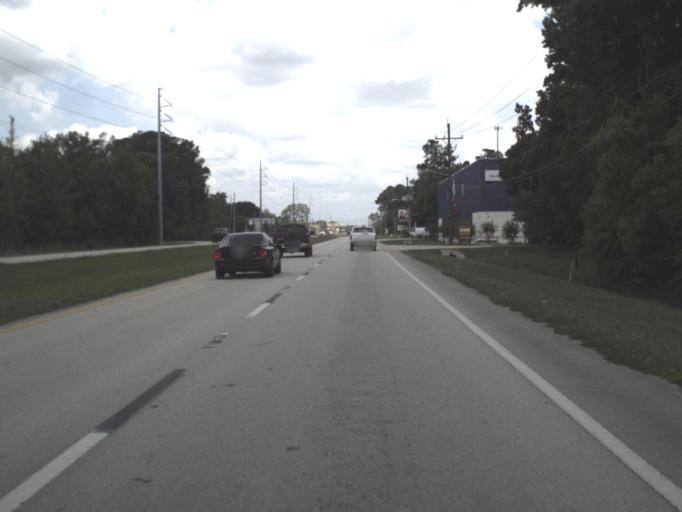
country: US
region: Florida
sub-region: Duval County
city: Jacksonville
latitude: 30.2535
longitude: -81.6079
